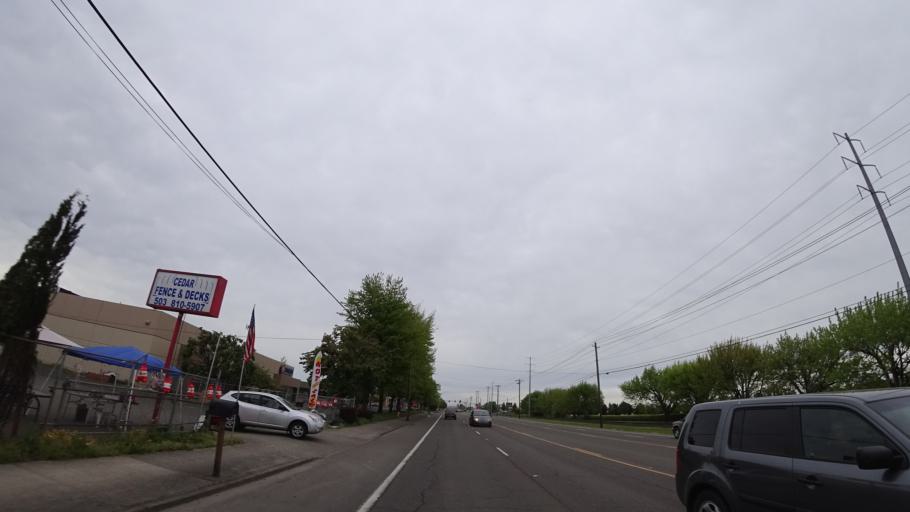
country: US
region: Oregon
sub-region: Washington County
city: Aloha
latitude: 45.4996
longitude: -122.9202
